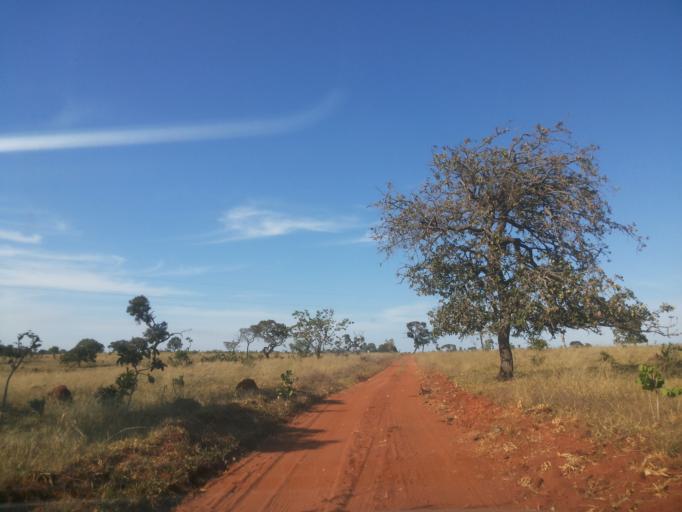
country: BR
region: Minas Gerais
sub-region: Ituiutaba
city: Ituiutaba
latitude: -19.1066
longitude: -49.4169
